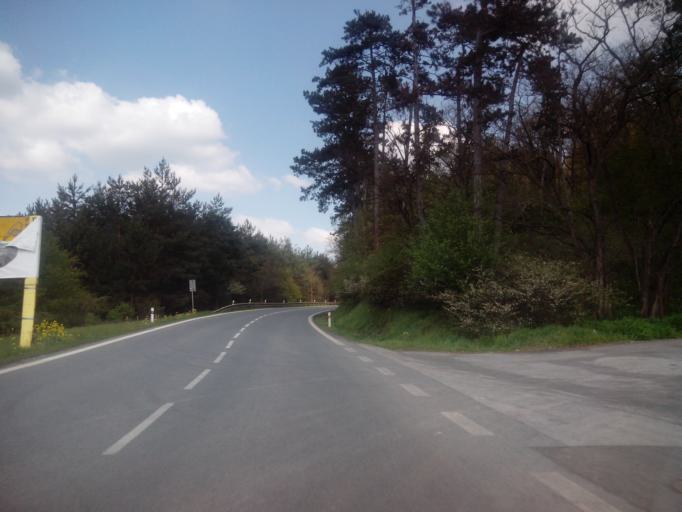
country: CZ
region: Central Bohemia
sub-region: Okres Beroun
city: Beroun
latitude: 49.9753
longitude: 14.1015
